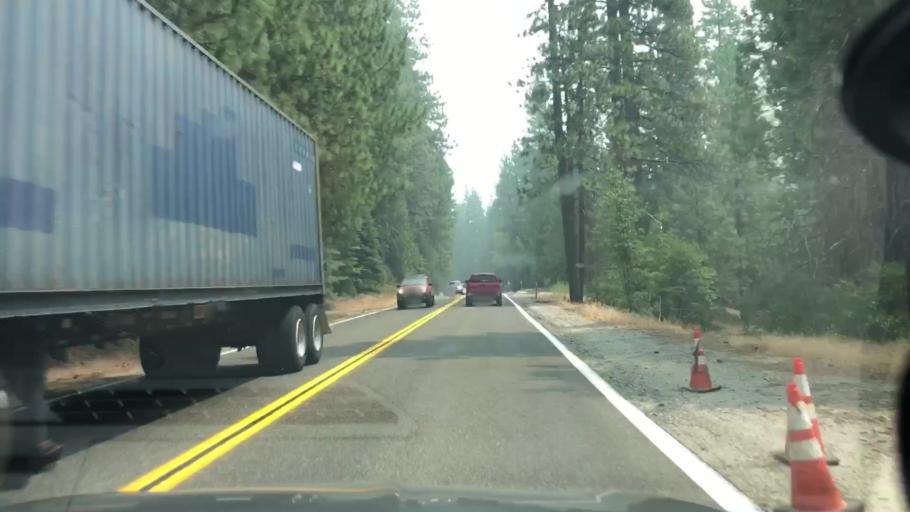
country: US
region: California
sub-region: El Dorado County
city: Pollock Pines
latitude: 38.7710
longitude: -120.3089
